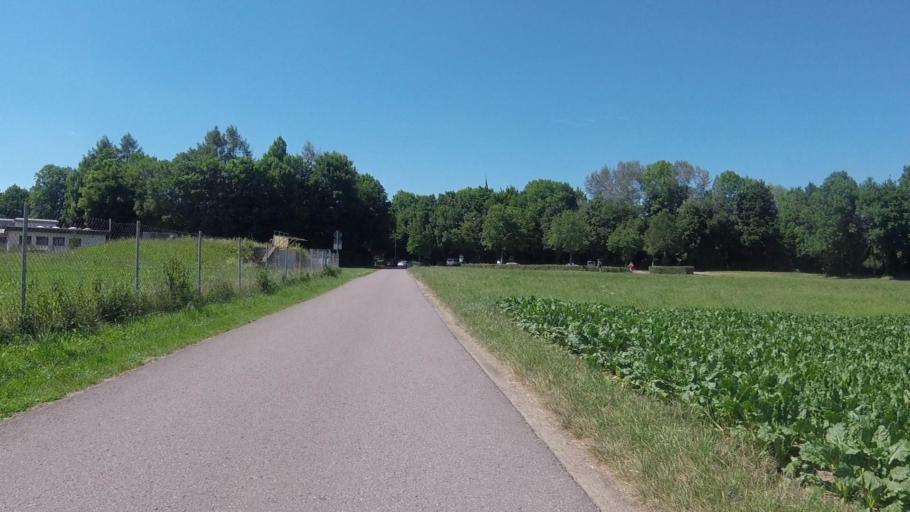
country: DE
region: Baden-Wuerttemberg
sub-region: Regierungsbezirk Stuttgart
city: Murr
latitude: 48.9616
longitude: 9.2636
